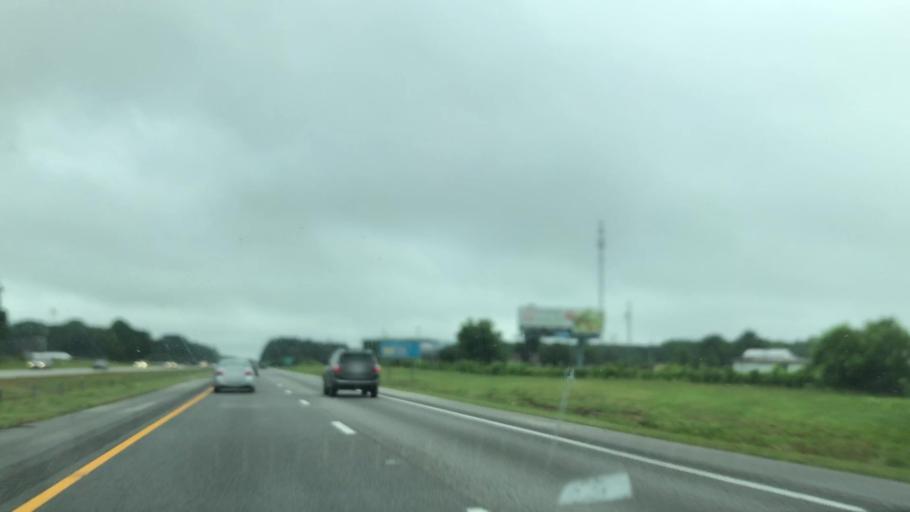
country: US
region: North Carolina
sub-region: Halifax County
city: Enfield
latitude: 36.2620
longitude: -77.7242
